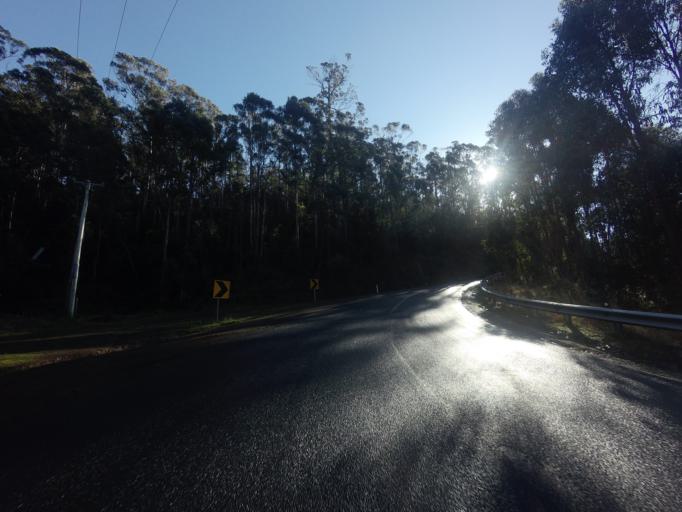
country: AU
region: Tasmania
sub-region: Glenorchy
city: Berriedale
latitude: -42.8259
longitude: 147.2067
